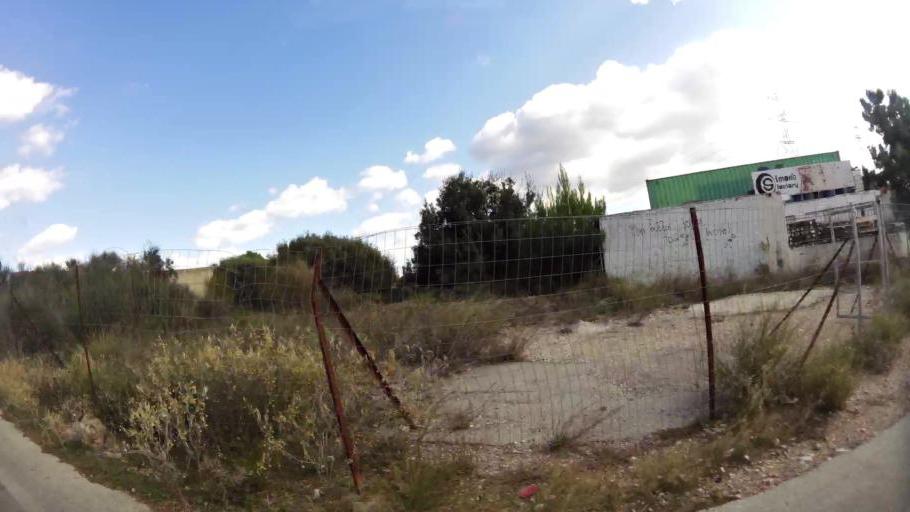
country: GR
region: Attica
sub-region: Nomarchia Anatolikis Attikis
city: Thrakomakedones
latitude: 38.1151
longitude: 23.7604
